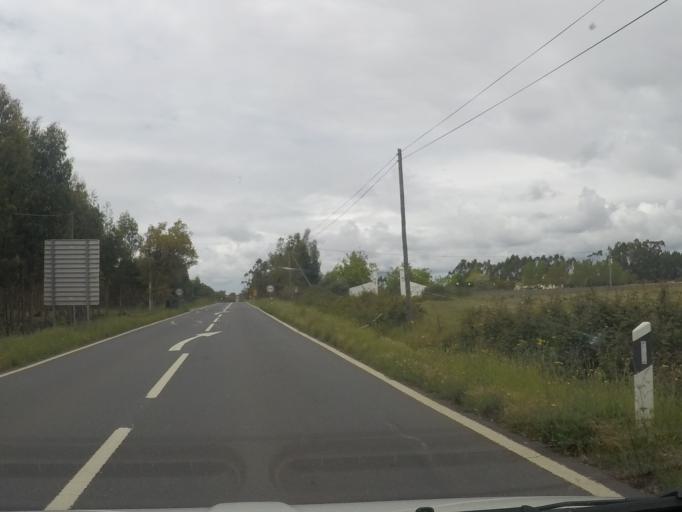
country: PT
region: Setubal
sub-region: Santiago do Cacem
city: Cercal
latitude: 37.8535
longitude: -8.7121
